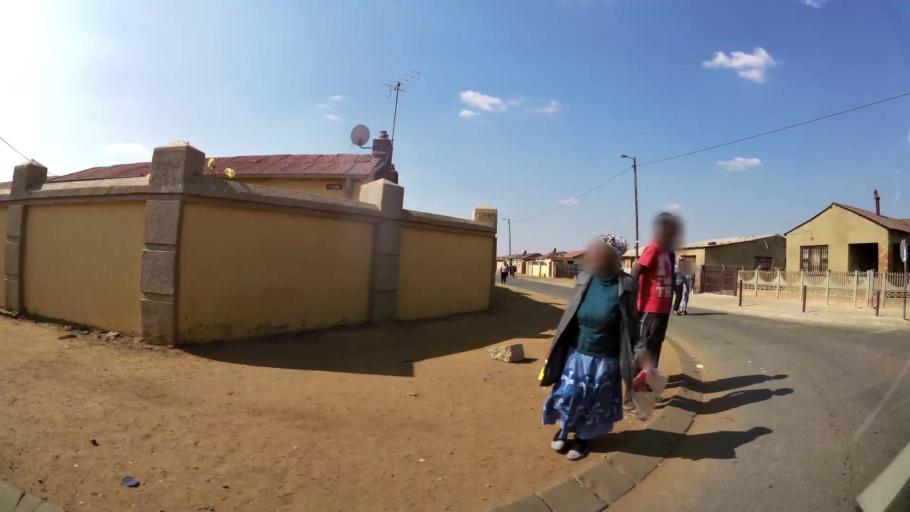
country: ZA
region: Gauteng
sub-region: Ekurhuleni Metropolitan Municipality
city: Benoni
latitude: -26.1487
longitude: 28.4050
